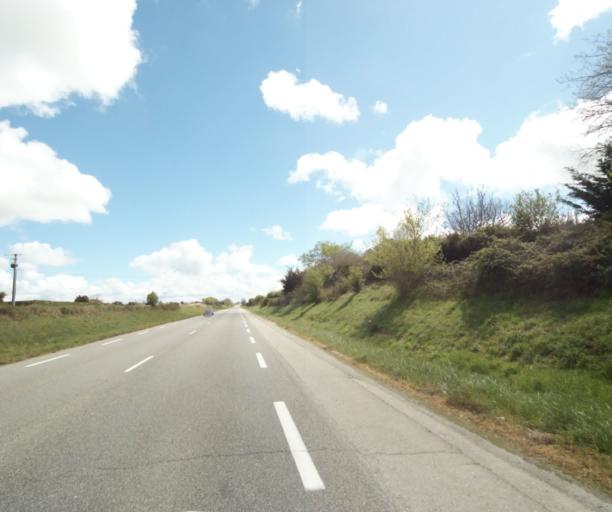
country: FR
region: Midi-Pyrenees
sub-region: Departement de l'Ariege
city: Saverdun
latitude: 43.2393
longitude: 1.5877
